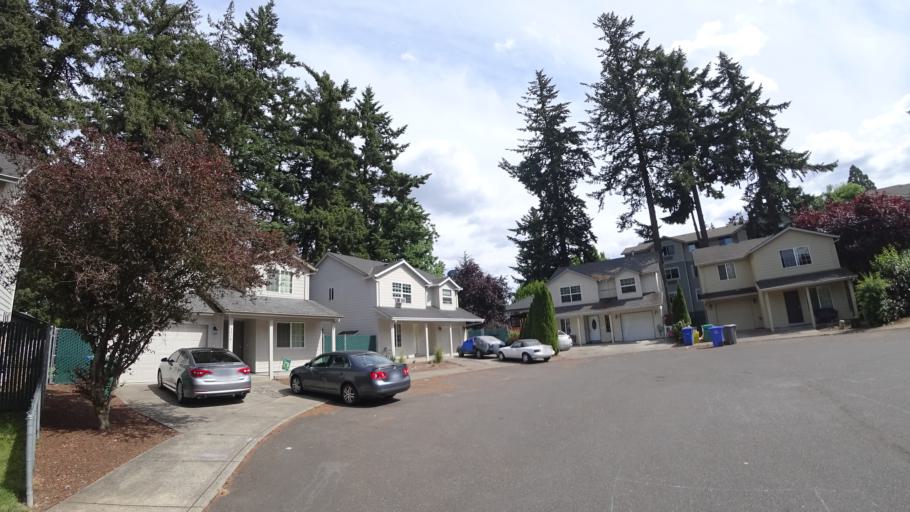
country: US
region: Oregon
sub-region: Multnomah County
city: Lents
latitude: 45.4936
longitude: -122.5421
